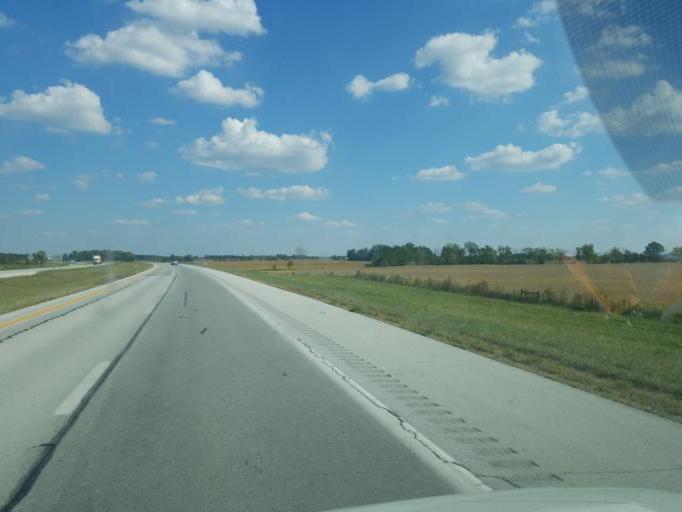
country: US
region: Ohio
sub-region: Hardin County
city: Forest
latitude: 40.8257
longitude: -83.4758
